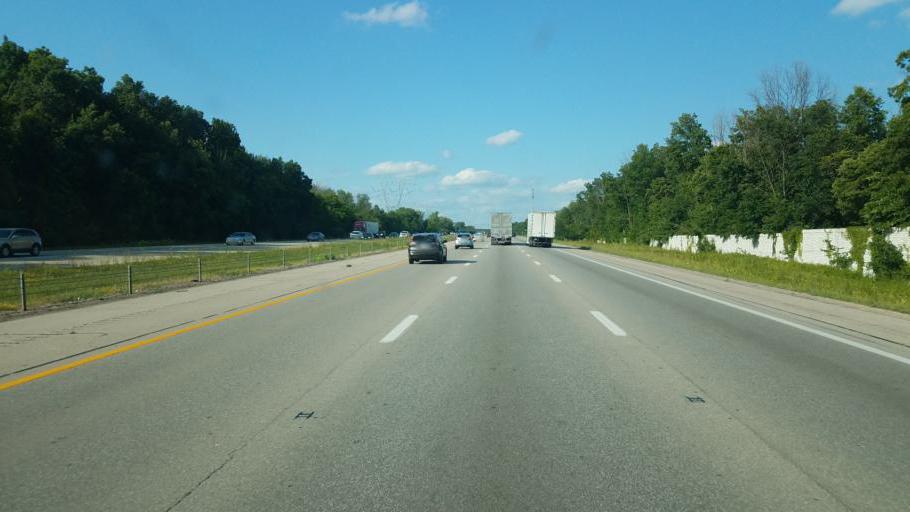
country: US
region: Ohio
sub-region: Franklin County
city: Westerville
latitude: 40.1853
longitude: -82.9459
